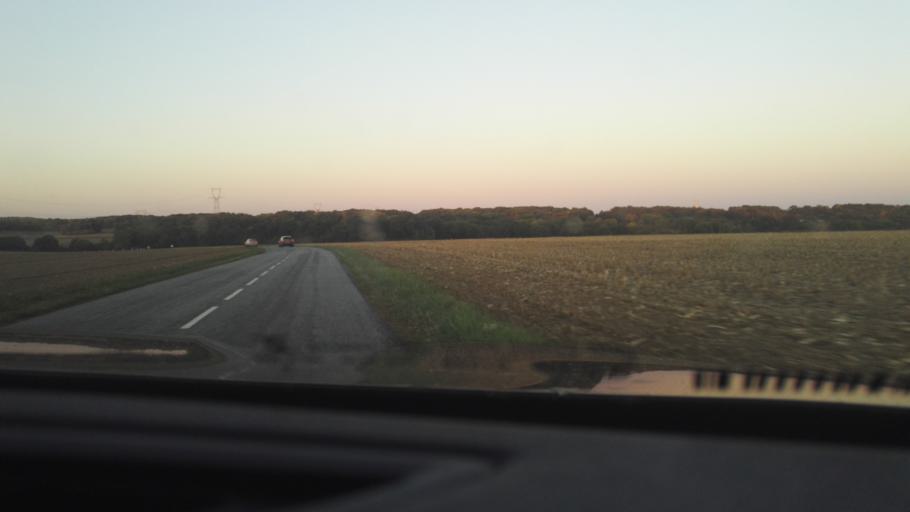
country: FR
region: Ile-de-France
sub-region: Departement des Yvelines
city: Longnes
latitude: 48.9023
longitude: 1.5854
